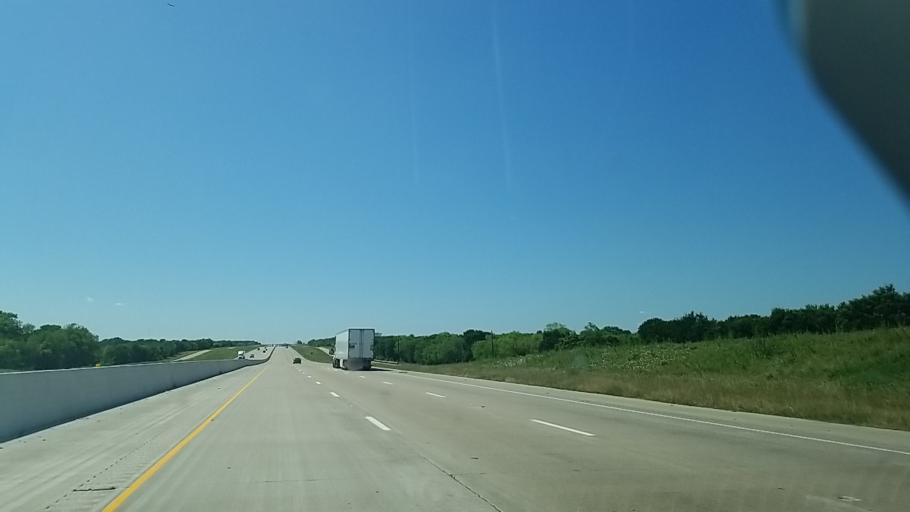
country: US
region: Texas
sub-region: Freestone County
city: Wortham
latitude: 31.8939
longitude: -96.3631
